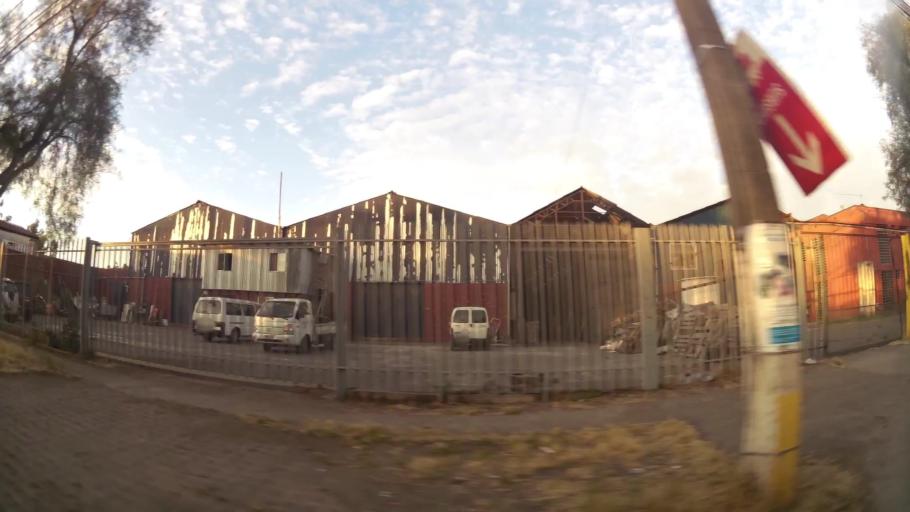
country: CL
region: Santiago Metropolitan
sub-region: Provincia de Maipo
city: San Bernardo
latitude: -33.6193
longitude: -70.6940
